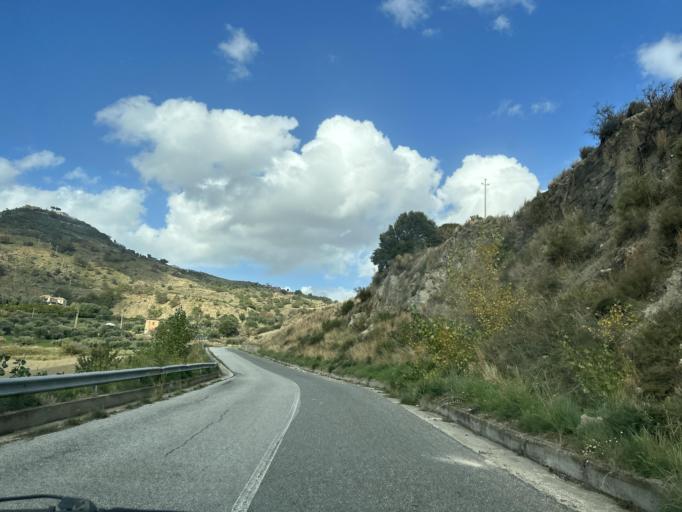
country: IT
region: Calabria
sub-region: Provincia di Catanzaro
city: Gasperina
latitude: 38.7243
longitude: 16.5189
